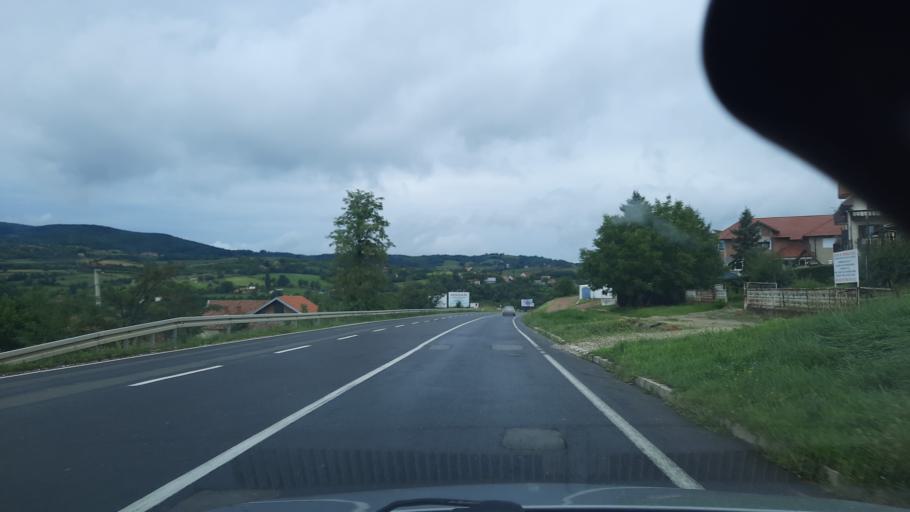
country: RS
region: Central Serbia
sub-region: Sumadijski Okrug
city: Kragujevac
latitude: 43.9793
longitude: 20.8288
